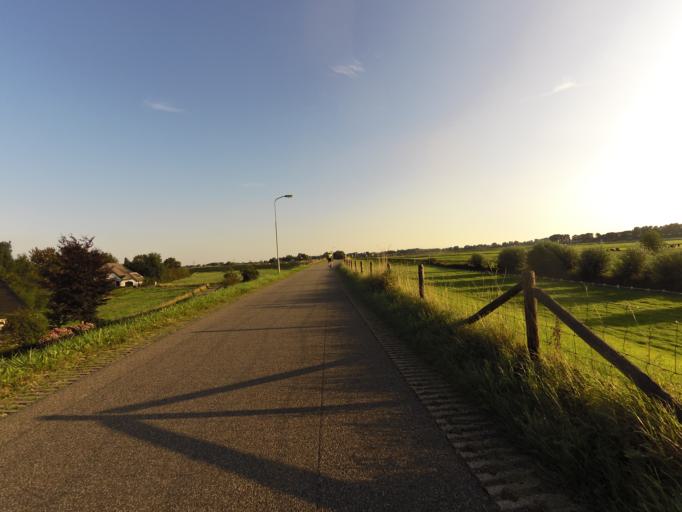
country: NL
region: Gelderland
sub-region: Gemeente Westervoort
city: Westervoort
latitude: 51.9371
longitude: 5.9690
